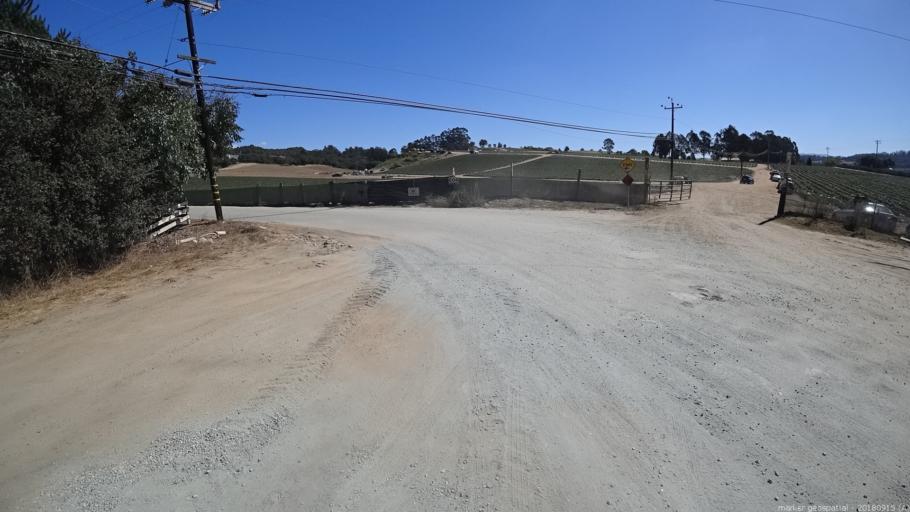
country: US
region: California
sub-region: Monterey County
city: Las Lomas
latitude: 36.8651
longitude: -121.7138
